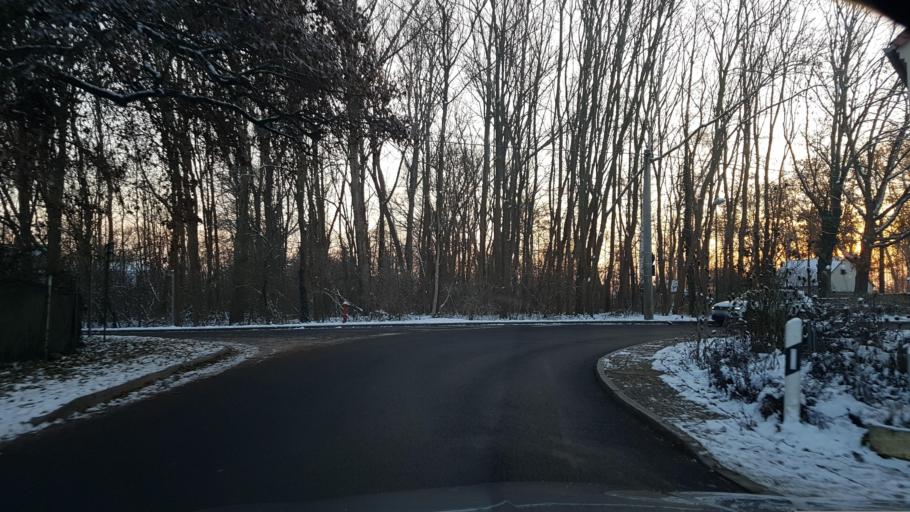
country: DE
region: Saxony
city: Taucha
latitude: 51.4263
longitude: 12.4800
